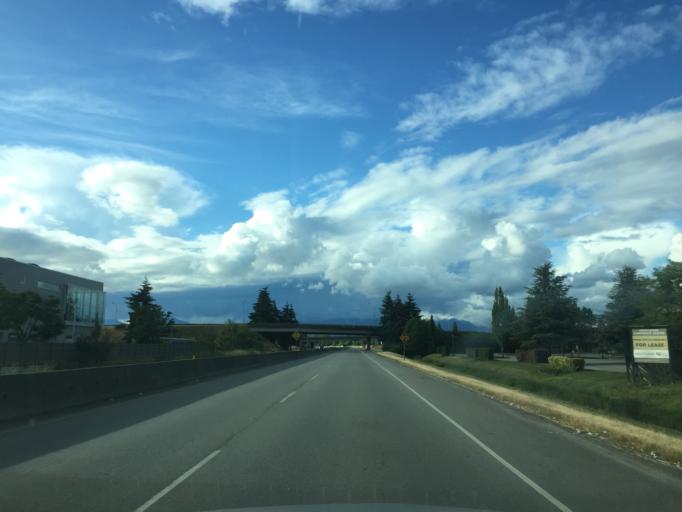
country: CA
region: British Columbia
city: Richmond
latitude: 49.1737
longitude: -123.0744
